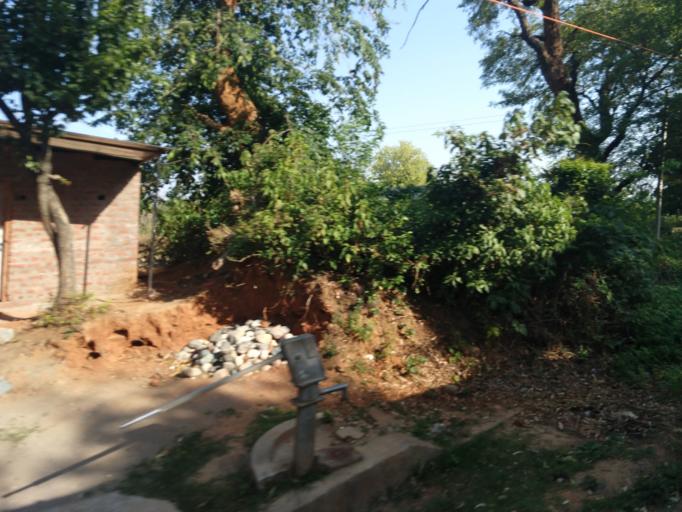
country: IN
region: Himachal Pradesh
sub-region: Chamba
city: Chowari
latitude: 32.3725
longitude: 75.9233
